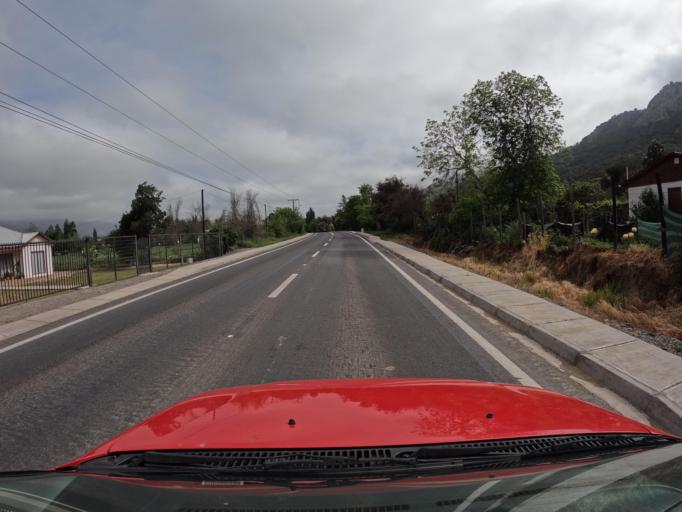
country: CL
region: Maule
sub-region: Provincia de Curico
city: Teno
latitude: -34.8132
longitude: -71.2132
